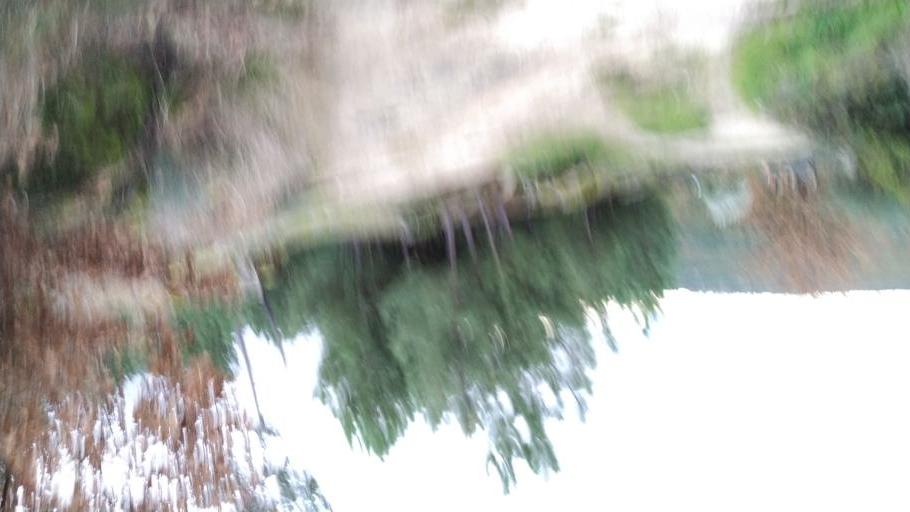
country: PT
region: Vila Real
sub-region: Vila Real
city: Vila Real
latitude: 41.3518
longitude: -7.7139
